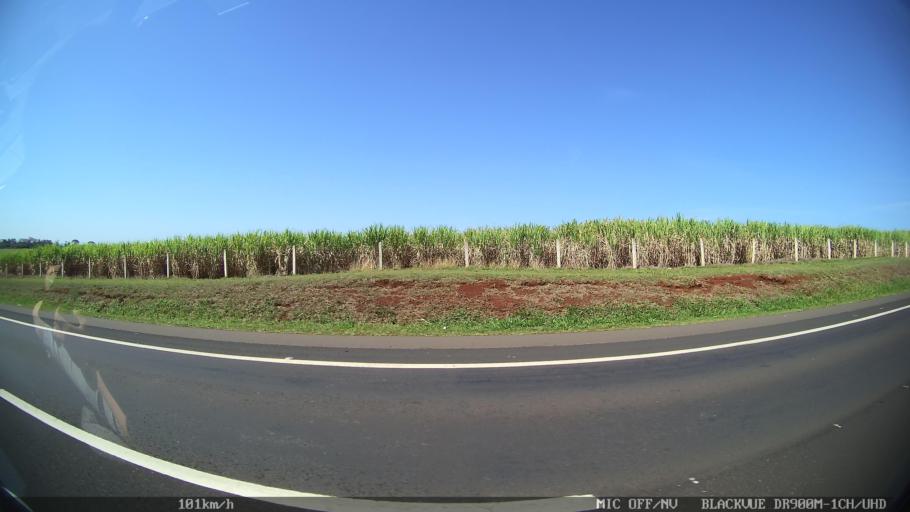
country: BR
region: Sao Paulo
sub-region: Batatais
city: Batatais
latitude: -20.7910
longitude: -47.5603
